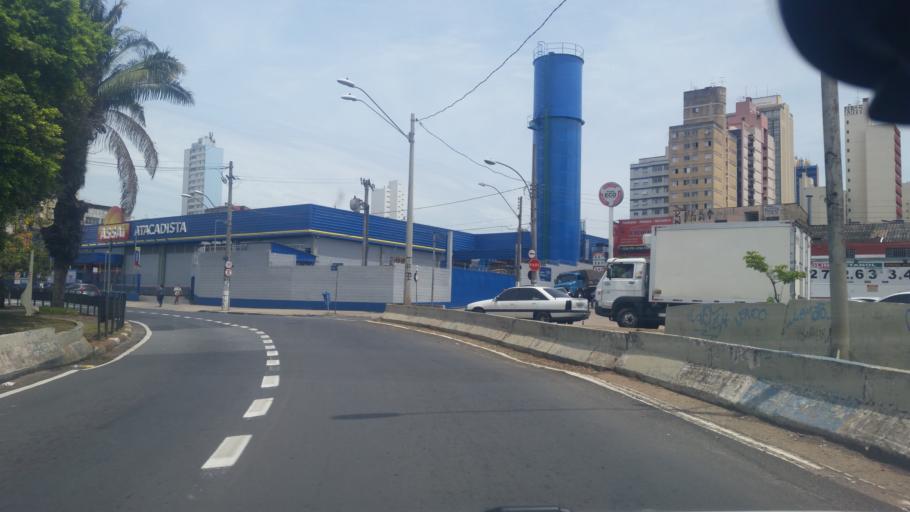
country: BR
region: Sao Paulo
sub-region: Campinas
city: Campinas
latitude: -22.9033
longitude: -47.0653
